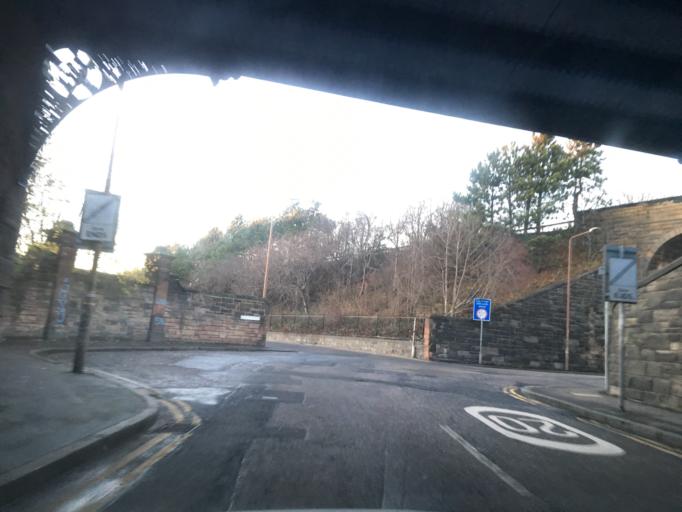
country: GB
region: Scotland
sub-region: Edinburgh
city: Edinburgh
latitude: 55.9408
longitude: -3.2280
